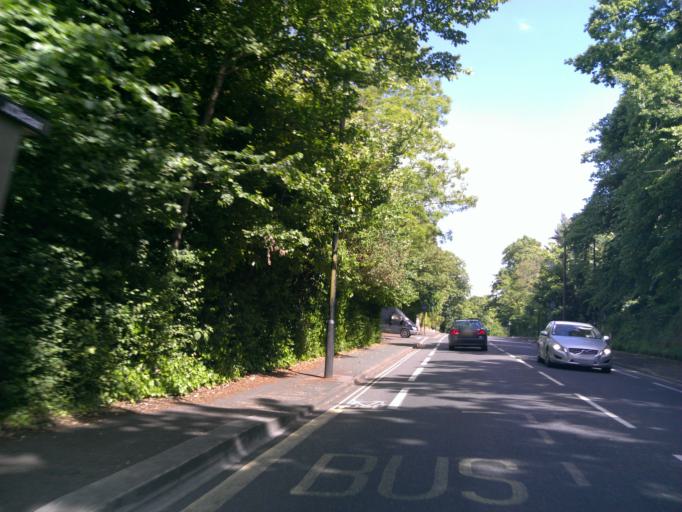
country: GB
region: England
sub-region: Essex
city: West Bergholt
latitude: 51.8901
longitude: 0.8690
